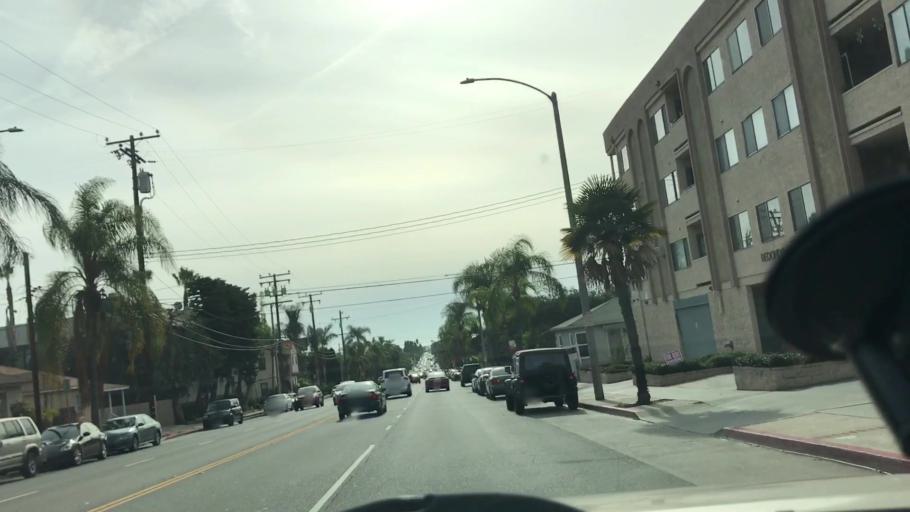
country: US
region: California
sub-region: Los Angeles County
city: Signal Hill
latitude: 33.7875
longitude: -118.1525
